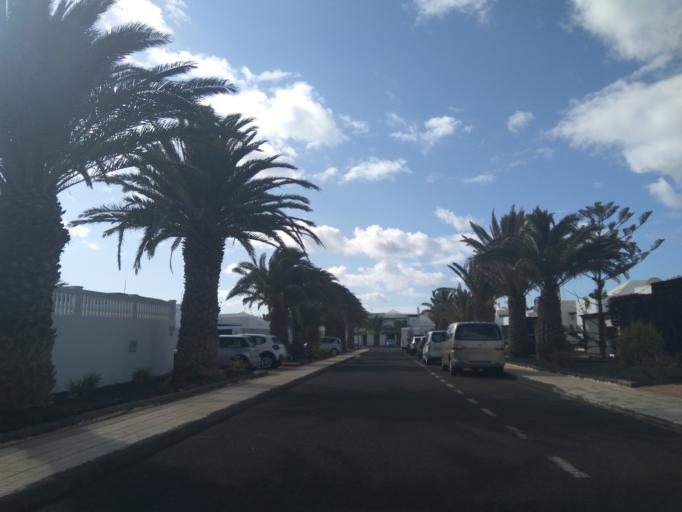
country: ES
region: Canary Islands
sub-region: Provincia de Las Palmas
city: Arrecife
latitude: 29.0067
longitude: -13.4891
